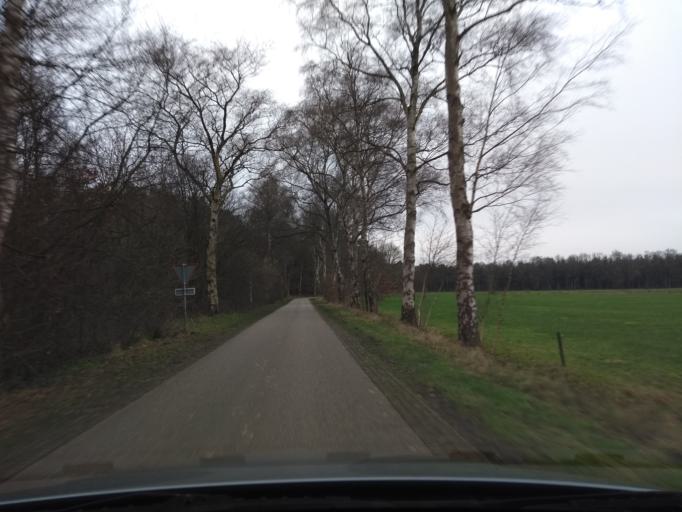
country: NL
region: Gelderland
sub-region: Gemeente Lochem
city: Barchem
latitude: 52.0720
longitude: 6.3953
